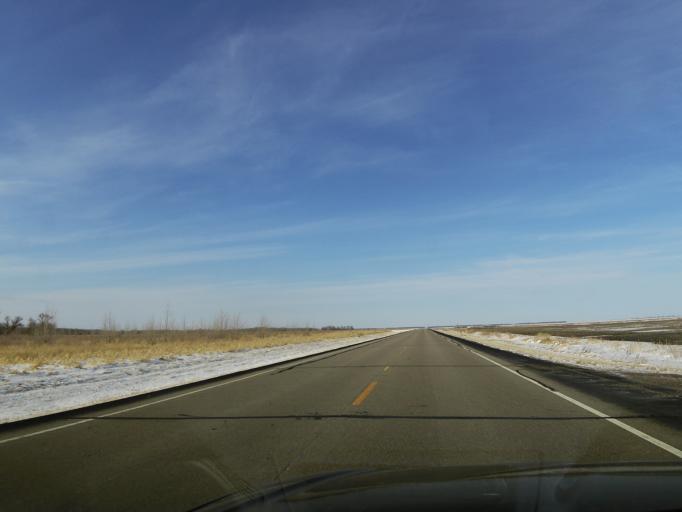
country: US
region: North Dakota
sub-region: Walsh County
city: Grafton
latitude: 48.4248
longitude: -97.1072
